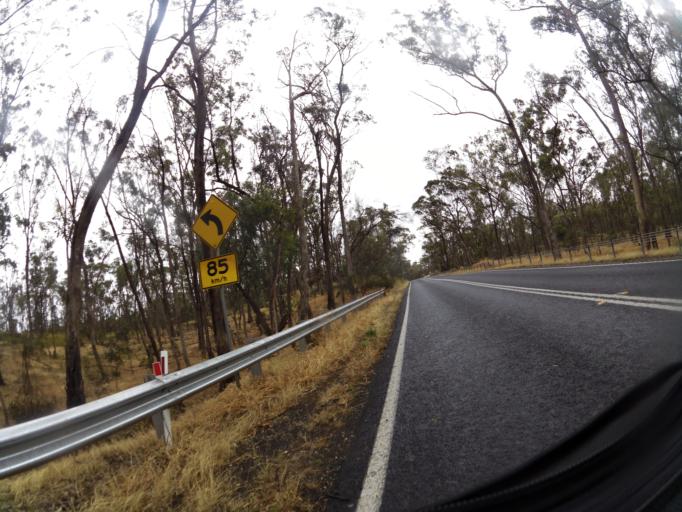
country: AU
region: Victoria
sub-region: Mount Alexander
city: Castlemaine
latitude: -37.1048
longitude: 144.1053
